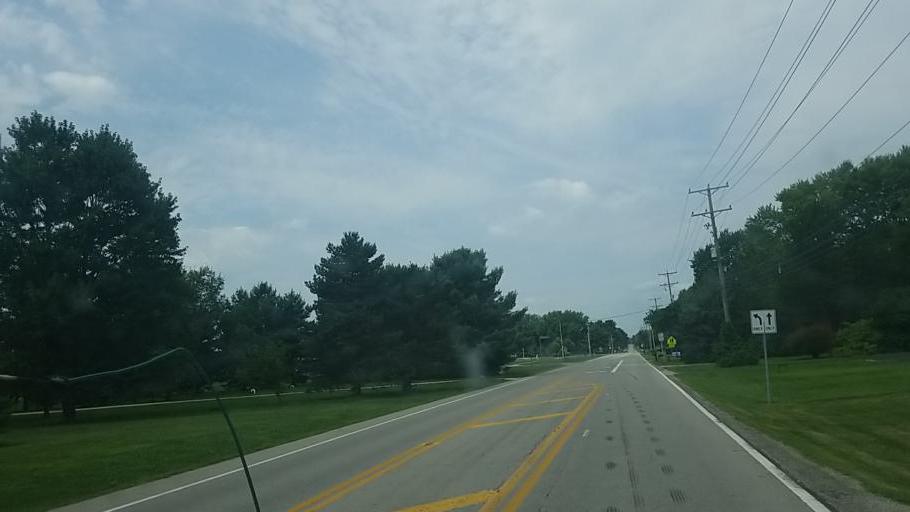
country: US
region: Ohio
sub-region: Franklin County
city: New Albany
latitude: 40.1134
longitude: -82.8239
